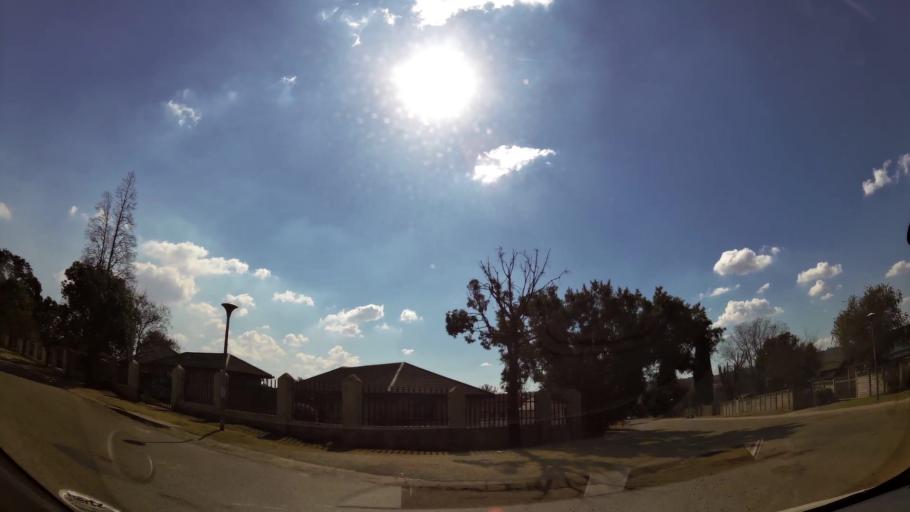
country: ZA
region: Mpumalanga
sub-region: Nkangala District Municipality
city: Witbank
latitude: -25.9440
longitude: 29.2488
